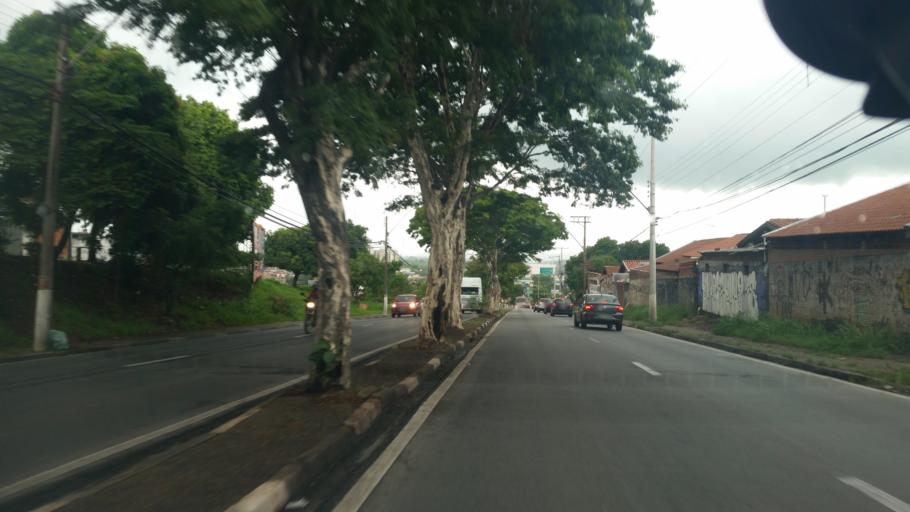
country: BR
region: Sao Paulo
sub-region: Campinas
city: Campinas
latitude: -22.9203
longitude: -47.1133
